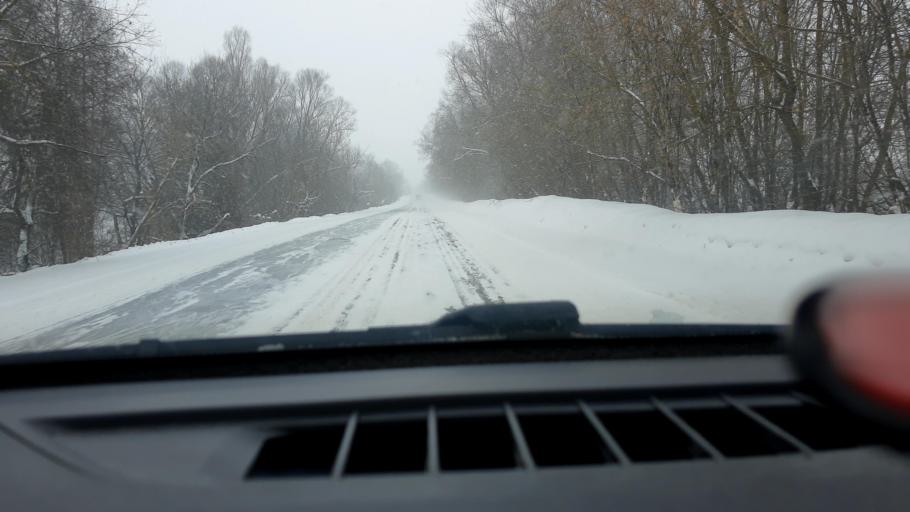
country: RU
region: Nizjnij Novgorod
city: Buturlino
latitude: 55.5802
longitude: 44.9131
